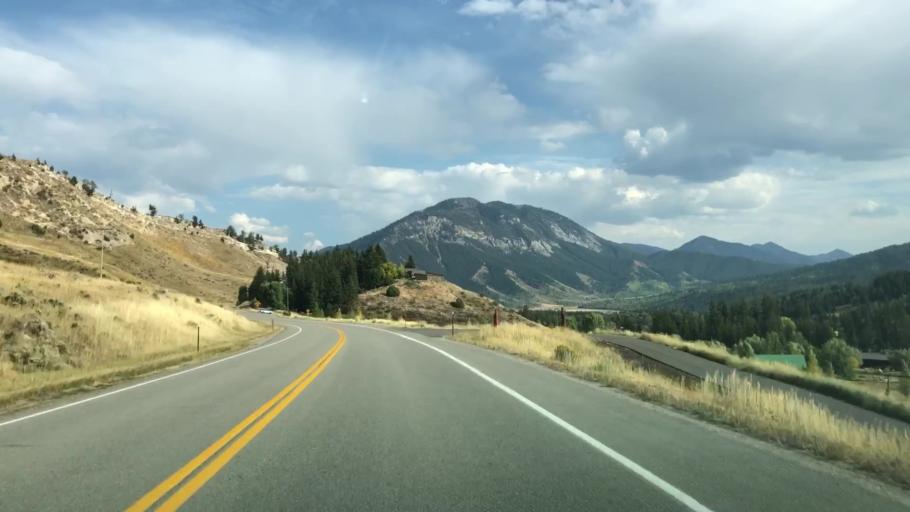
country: US
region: Wyoming
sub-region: Teton County
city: Hoback
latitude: 43.3098
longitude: -110.6809
